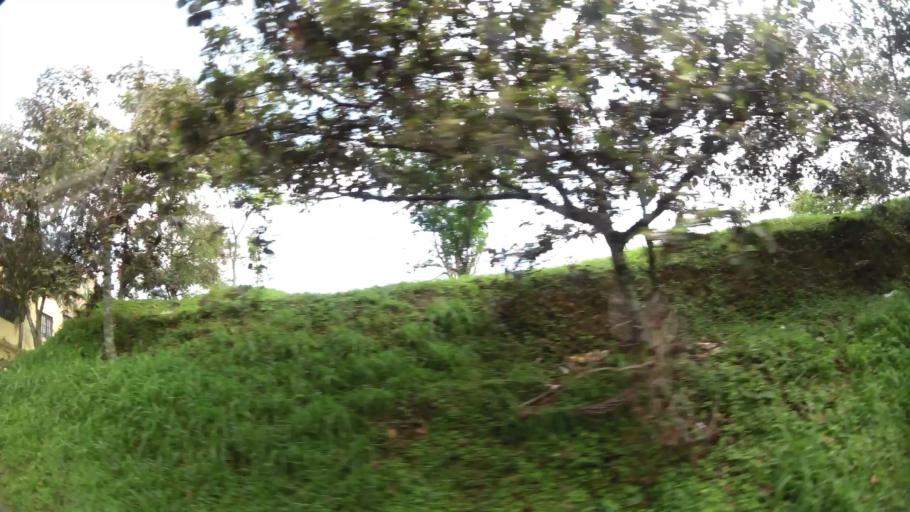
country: CO
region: Antioquia
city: La Estrella
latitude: 6.1750
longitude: -75.6411
